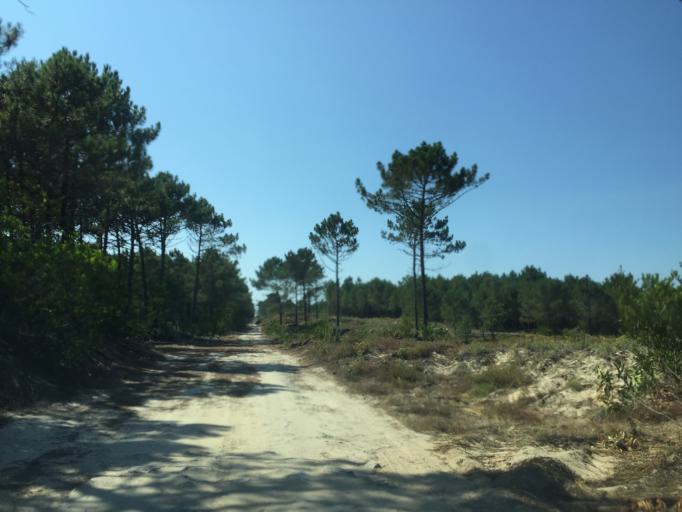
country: PT
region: Coimbra
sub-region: Figueira da Foz
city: Tavarede
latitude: 40.2610
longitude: -8.8531
